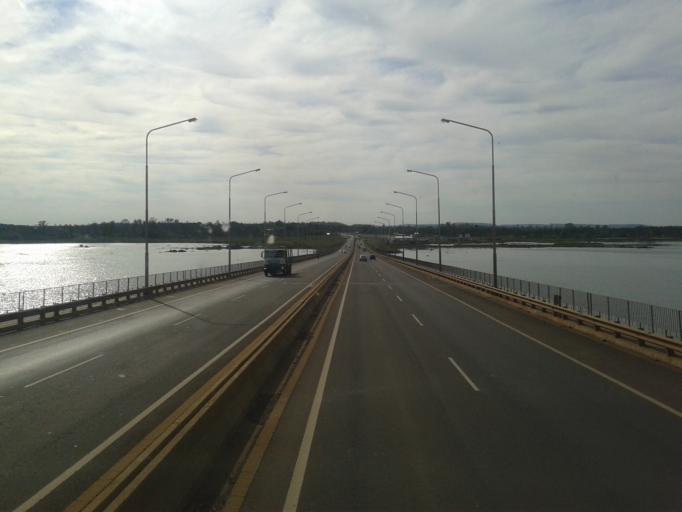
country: AR
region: Misiones
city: Garupa
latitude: -27.4628
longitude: -55.8152
